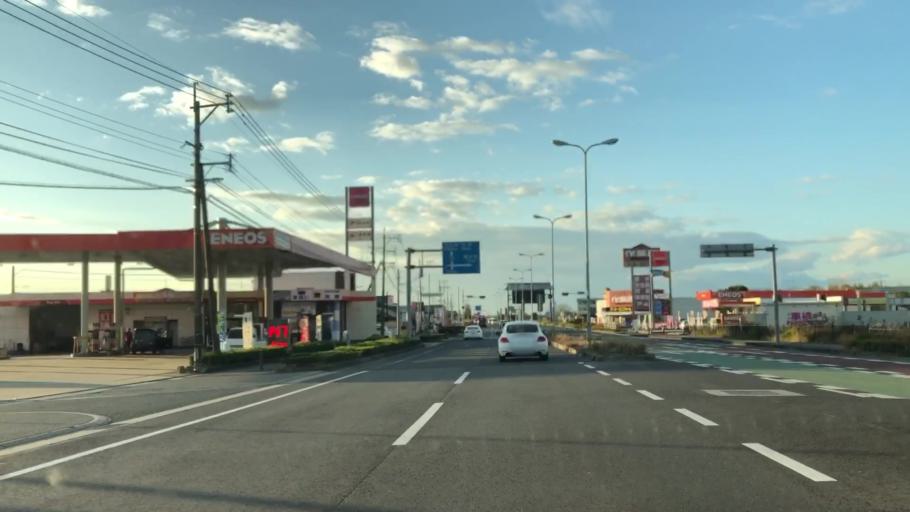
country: JP
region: Fukuoka
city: Nakatsu
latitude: 33.5393
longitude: 131.2947
